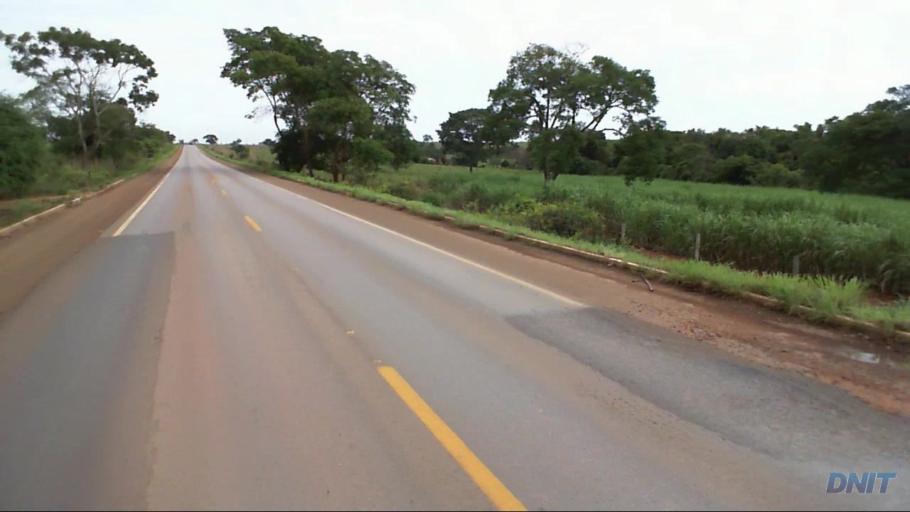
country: BR
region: Goias
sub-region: Uruacu
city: Uruacu
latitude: -14.7113
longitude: -49.1088
